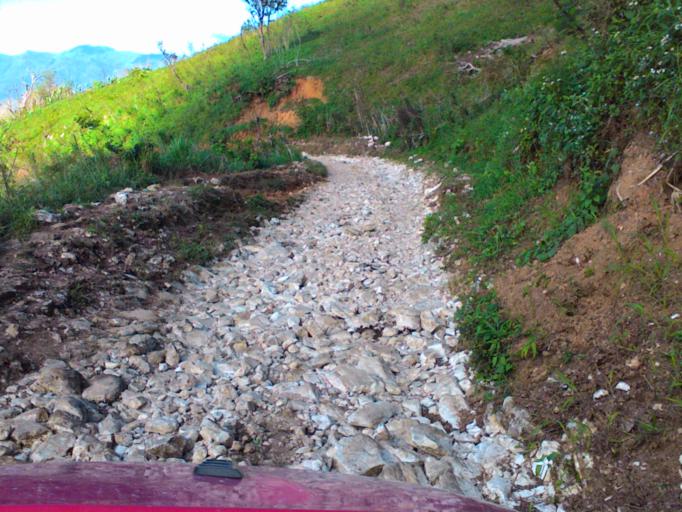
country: HT
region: Grandans
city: Moron
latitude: 18.4693
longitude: -74.1139
